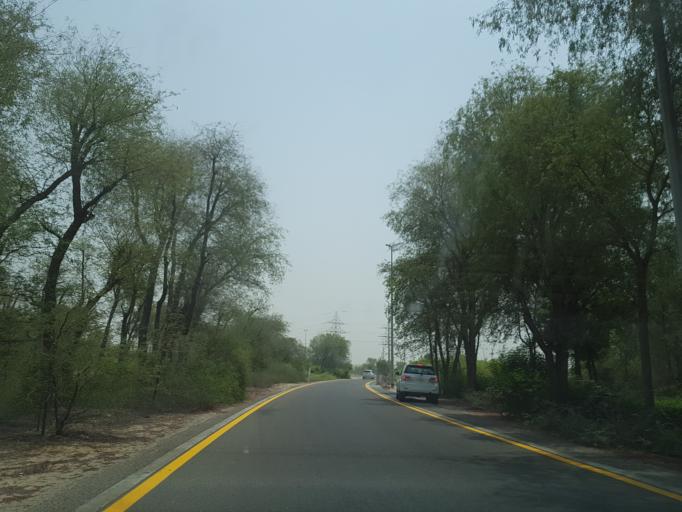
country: AE
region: Dubai
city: Dubai
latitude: 25.1496
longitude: 55.3389
